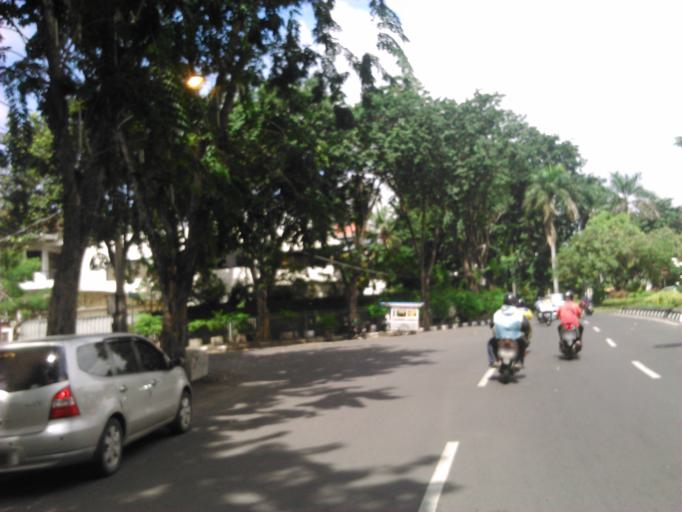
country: ID
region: East Java
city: Gubengairlangga
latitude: -7.2836
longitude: 112.7360
